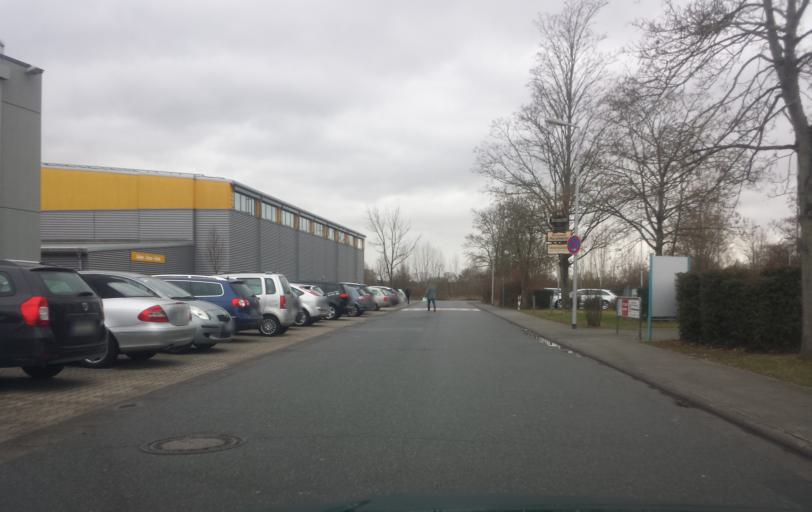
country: DE
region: Hesse
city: Weiterstadt
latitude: 49.9057
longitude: 8.5728
